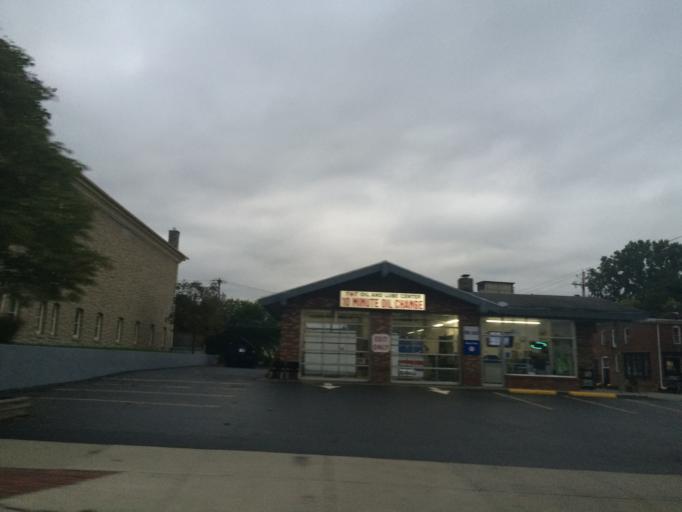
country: US
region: New York
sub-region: Erie County
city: East Aurora
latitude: 42.7679
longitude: -78.6112
